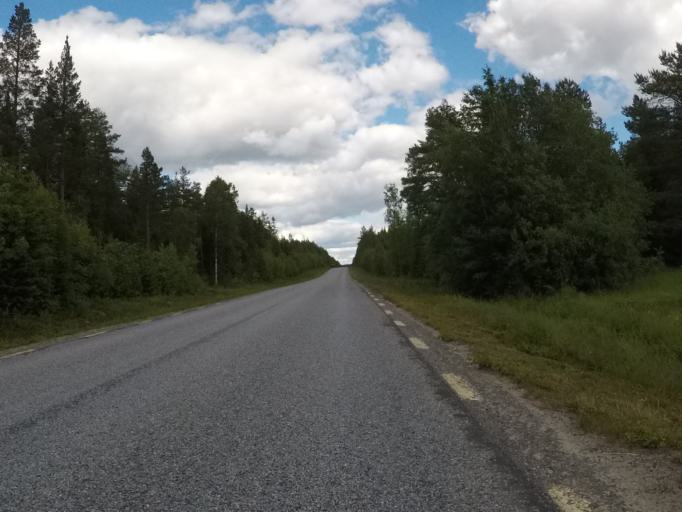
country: SE
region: Vaesterbotten
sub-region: Umea Kommun
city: Saevar
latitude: 63.9424
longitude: 20.7882
